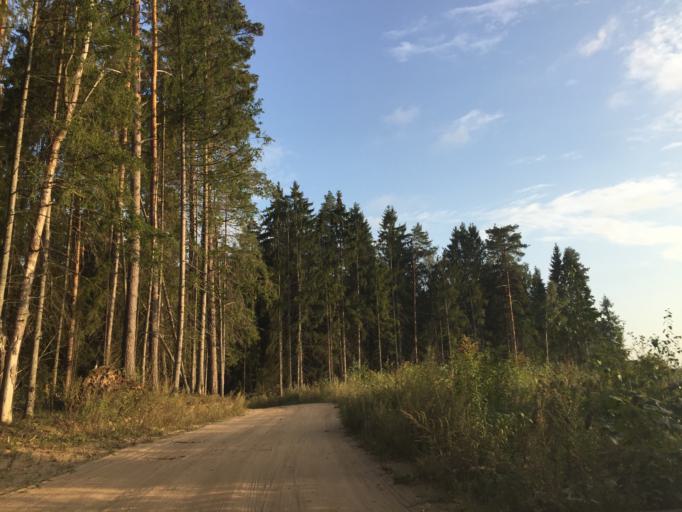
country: LV
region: Baldone
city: Baldone
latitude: 56.7615
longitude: 24.4096
